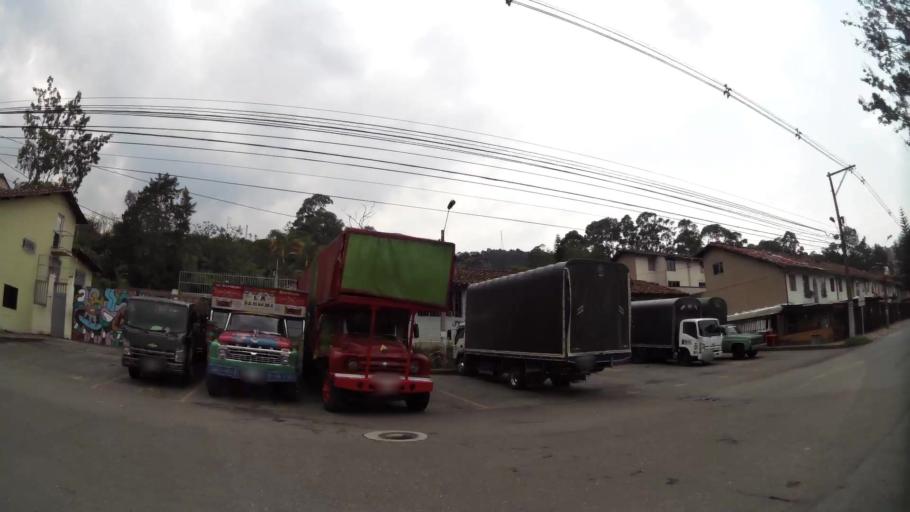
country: CO
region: Antioquia
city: Medellin
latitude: 6.2314
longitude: -75.5500
